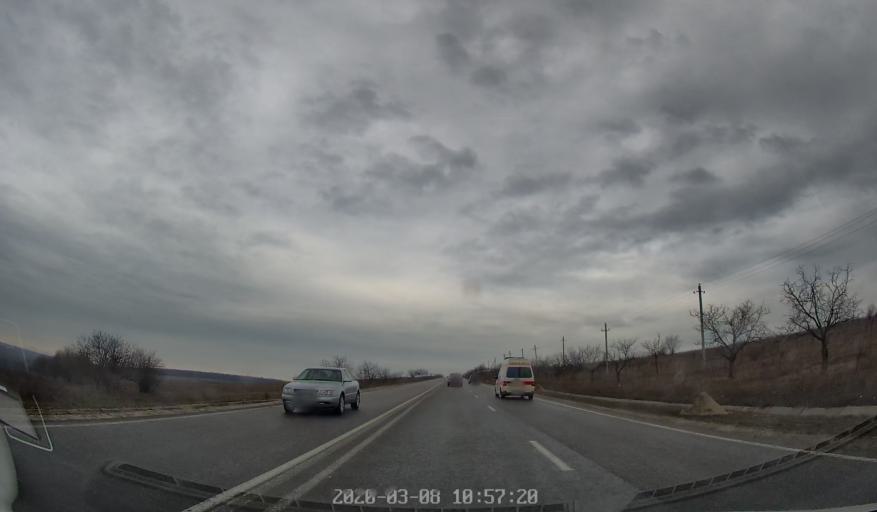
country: MD
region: Soldanesti
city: Soldanesti
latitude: 47.7108
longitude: 28.8473
